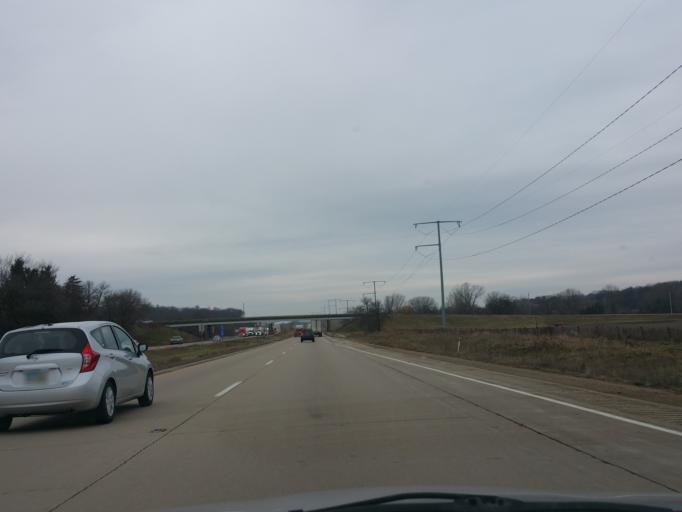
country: US
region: Wisconsin
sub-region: Dane County
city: Cottage Grove
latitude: 43.0039
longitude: -89.2069
